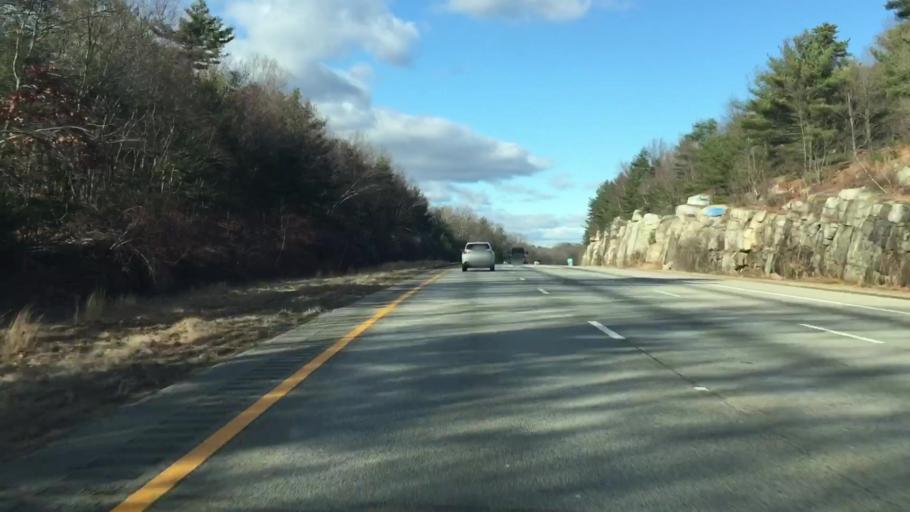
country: US
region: Massachusetts
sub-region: Middlesex County
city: Hopkinton
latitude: 42.1875
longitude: -71.5336
